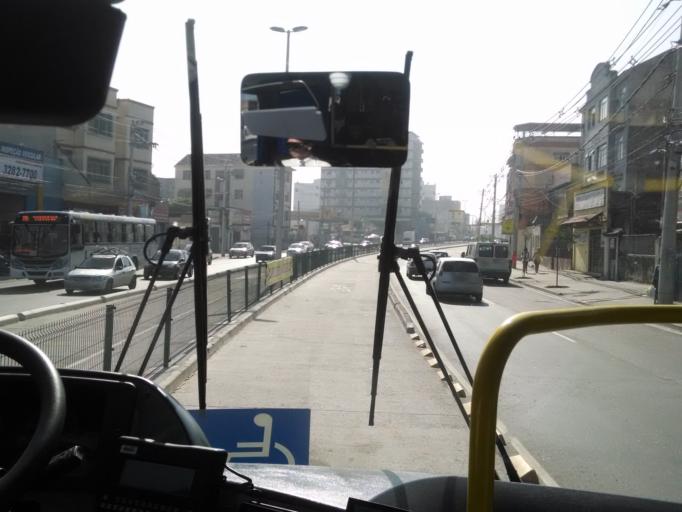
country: BR
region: Rio de Janeiro
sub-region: Sao Joao De Meriti
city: Sao Joao de Meriti
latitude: -22.8648
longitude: -43.3338
